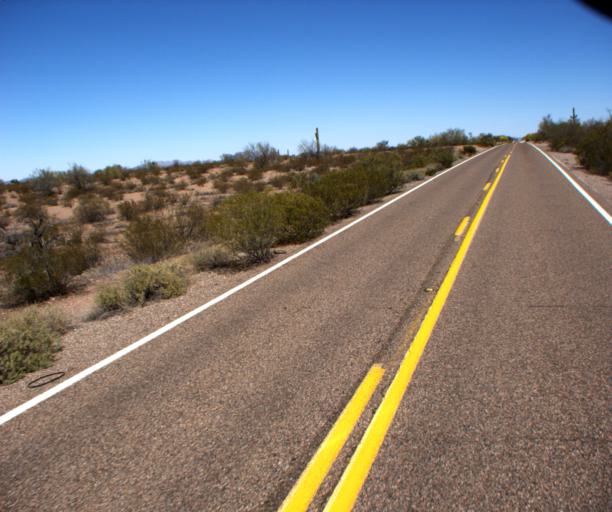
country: US
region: Arizona
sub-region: Pima County
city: Ajo
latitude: 32.1366
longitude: -112.7669
